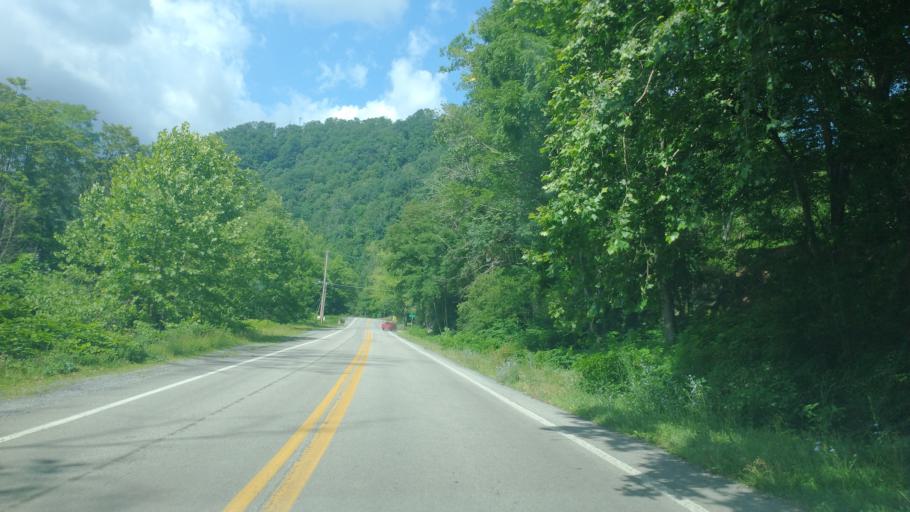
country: US
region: West Virginia
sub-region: McDowell County
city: Welch
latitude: 37.4304
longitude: -81.5068
